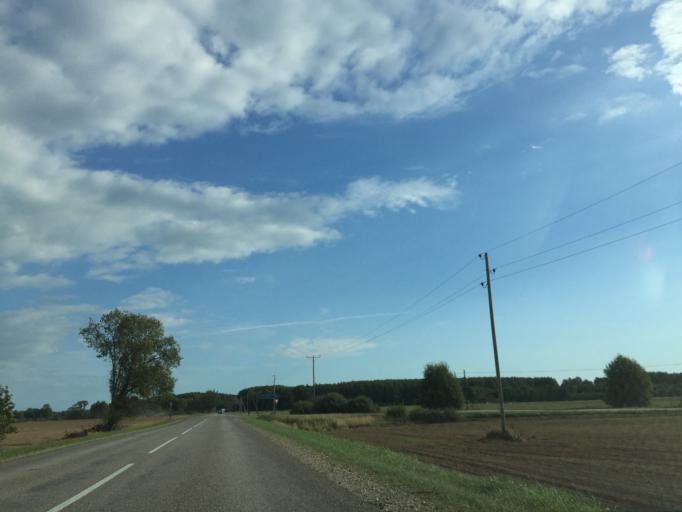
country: LV
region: Limbazu Rajons
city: Limbazi
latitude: 57.5111
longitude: 24.5135
